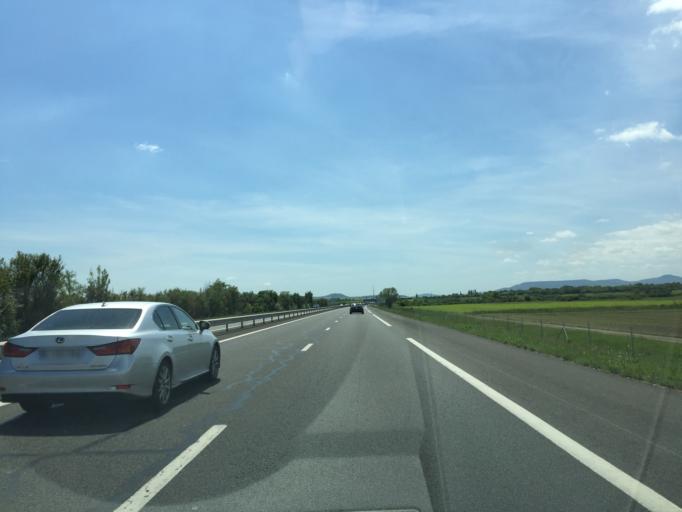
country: FR
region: Auvergne
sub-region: Departement du Puy-de-Dome
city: Gerzat
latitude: 45.8556
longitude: 3.1595
